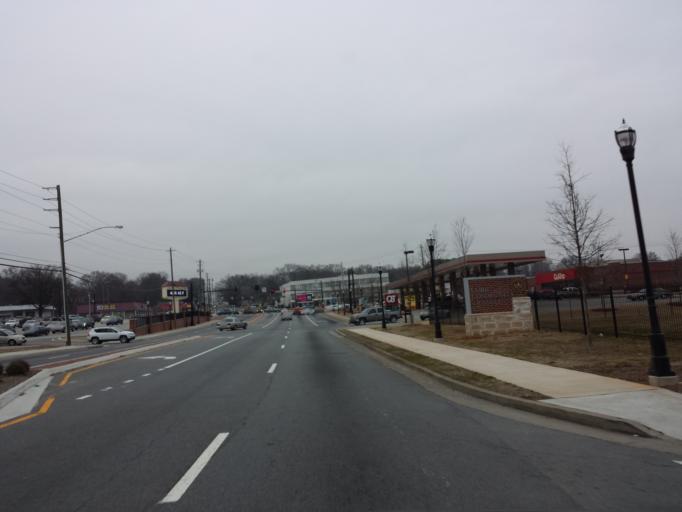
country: US
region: Georgia
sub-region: Cobb County
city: Marietta
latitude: 33.9417
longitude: -84.5350
